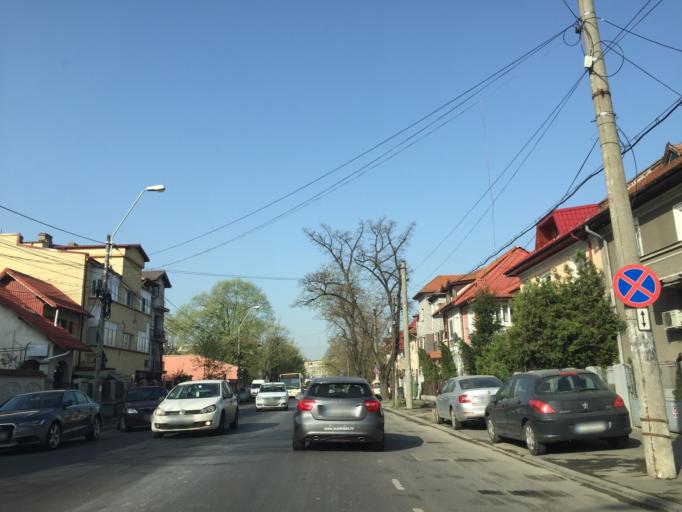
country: RO
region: Bucuresti
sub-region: Municipiul Bucuresti
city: Bucuresti
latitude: 44.4330
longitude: 26.0734
